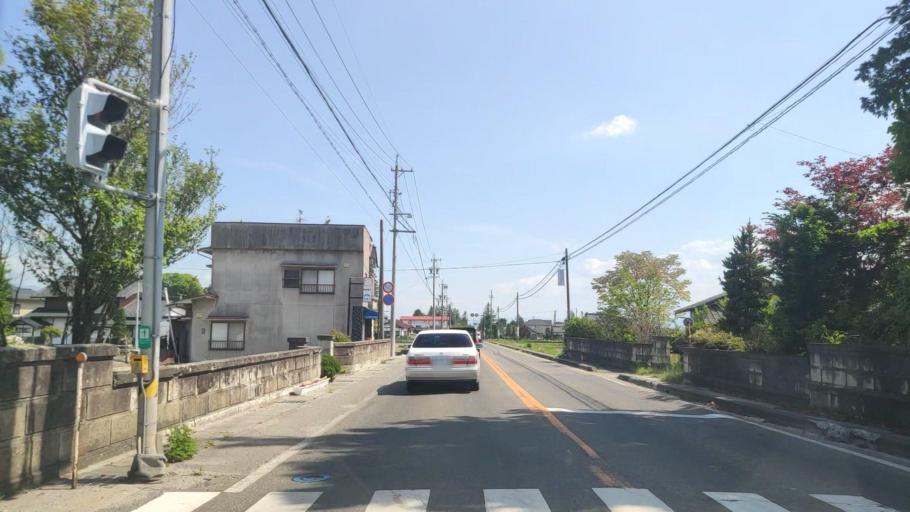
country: JP
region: Nagano
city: Hotaka
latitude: 36.3971
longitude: 137.8625
